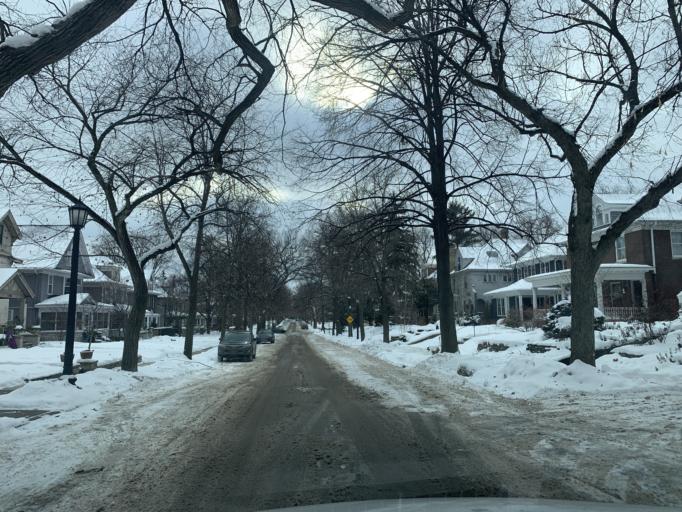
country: US
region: Minnesota
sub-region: Hennepin County
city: Minneapolis
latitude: 44.9622
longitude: -93.2982
